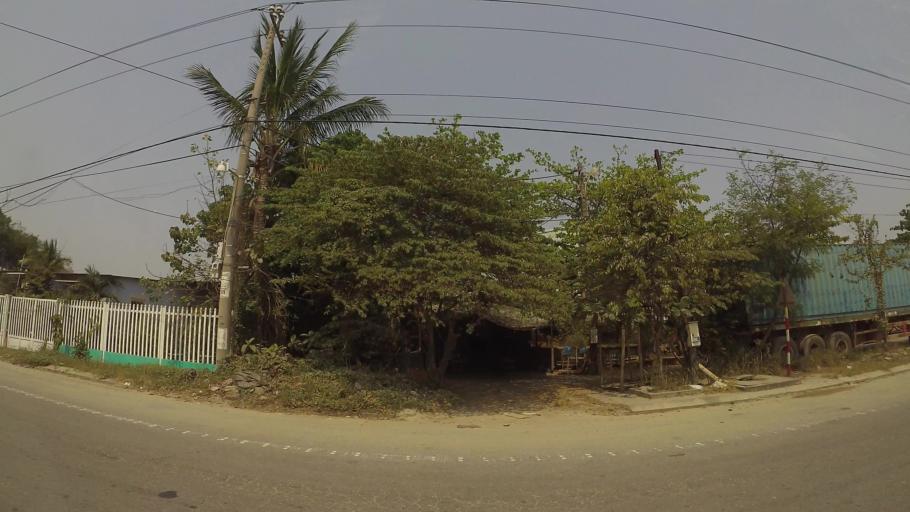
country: VN
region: Da Nang
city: Cam Le
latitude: 15.9859
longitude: 108.2019
